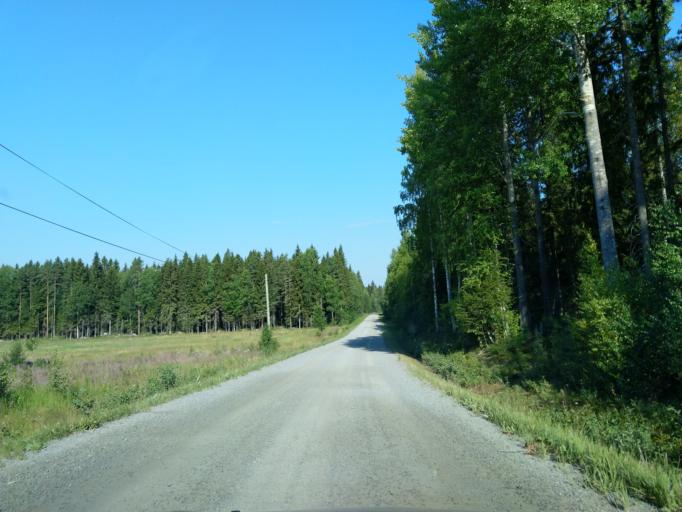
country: FI
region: Satakunta
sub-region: Pori
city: Laengelmaeki
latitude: 61.7308
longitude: 22.1786
